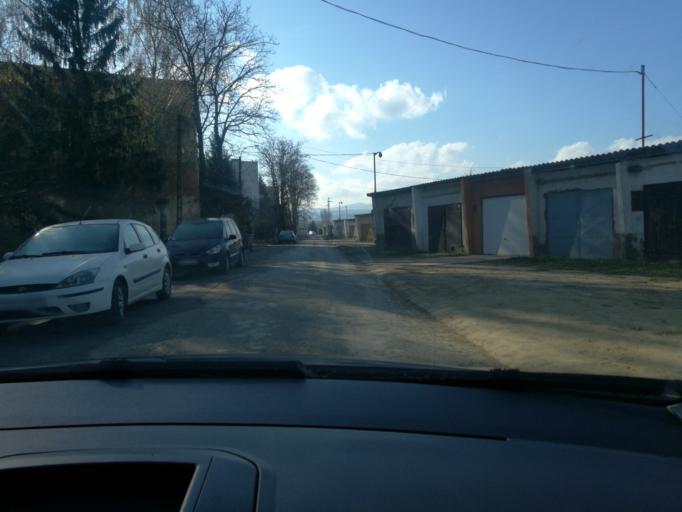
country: HU
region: Nograd
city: Batonyterenye
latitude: 47.9883
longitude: 19.8236
